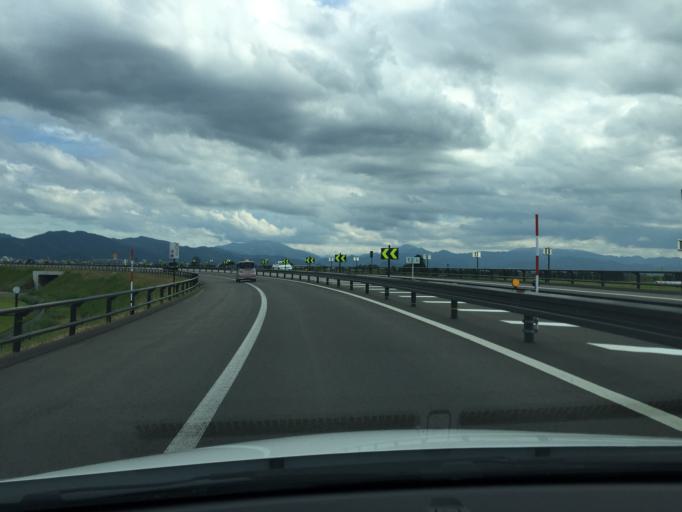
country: JP
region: Fukushima
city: Kitakata
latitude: 37.5398
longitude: 139.9081
